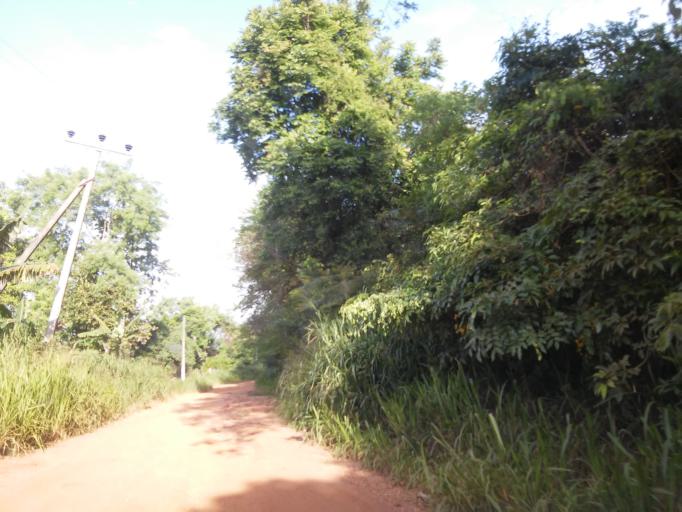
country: LK
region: Central
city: Sigiriya
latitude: 8.1718
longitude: 80.6753
